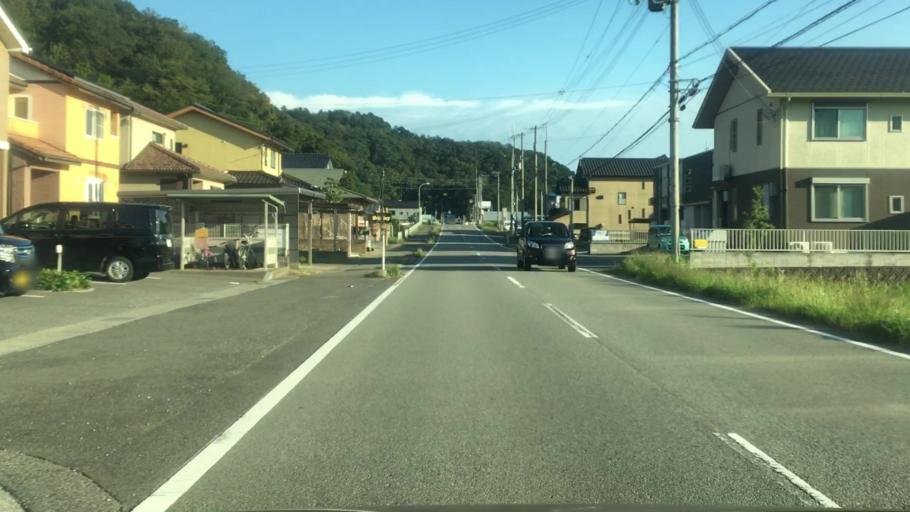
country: JP
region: Hyogo
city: Toyooka
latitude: 35.5620
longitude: 134.8220
